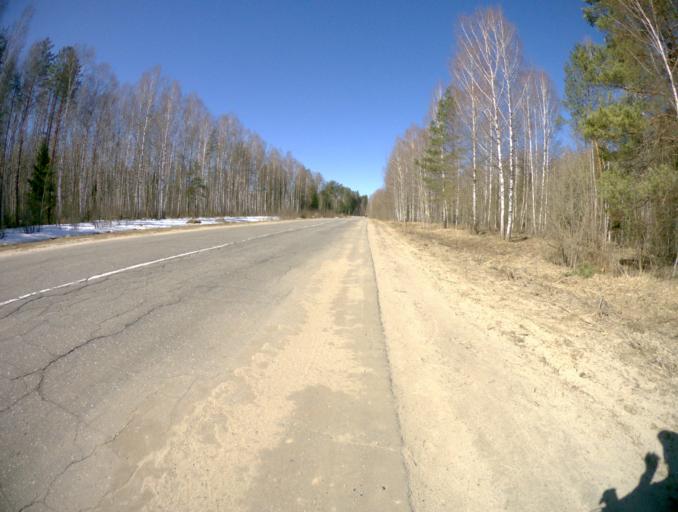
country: RU
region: Vladimir
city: Kameshkovo
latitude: 56.3483
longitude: 40.8490
